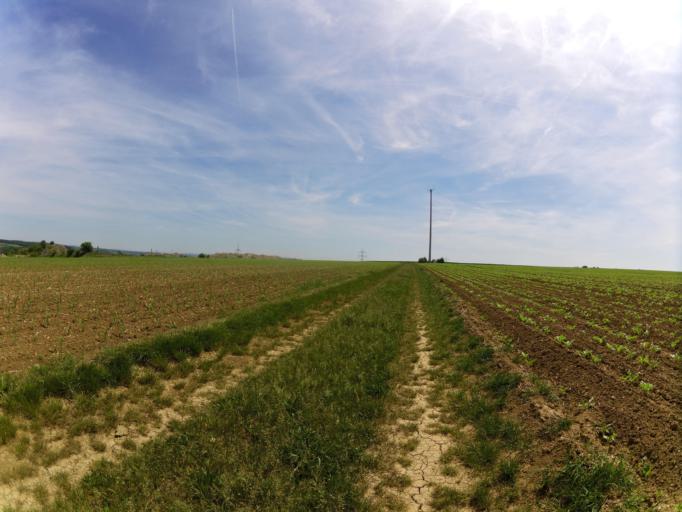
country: DE
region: Bavaria
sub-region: Regierungsbezirk Unterfranken
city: Sommerhausen
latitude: 49.6717
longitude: 10.0259
